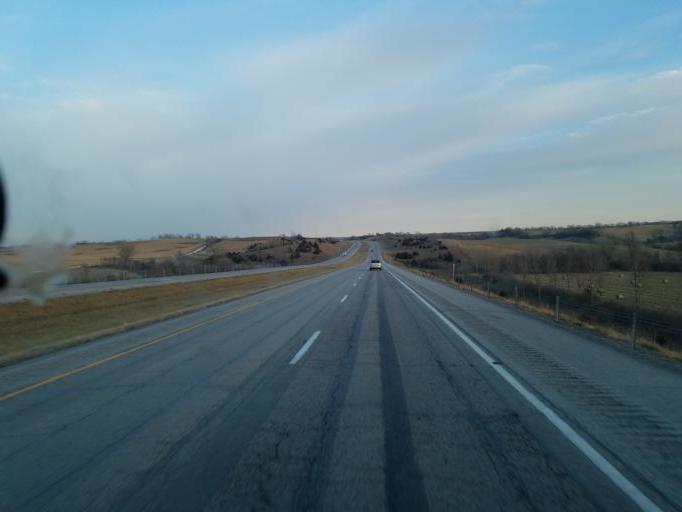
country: US
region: Iowa
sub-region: Harrison County
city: Missouri Valley
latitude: 41.4935
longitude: -95.8303
